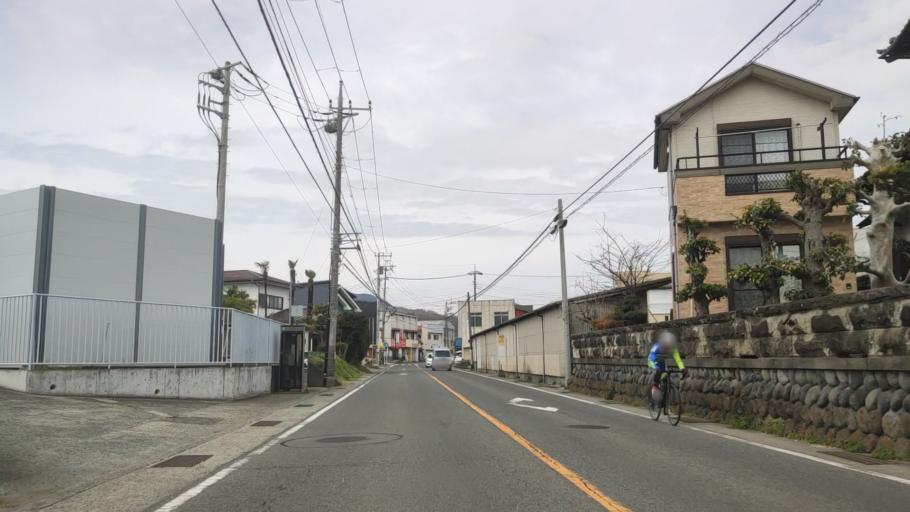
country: JP
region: Kanagawa
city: Ninomiya
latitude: 35.2993
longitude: 139.2295
